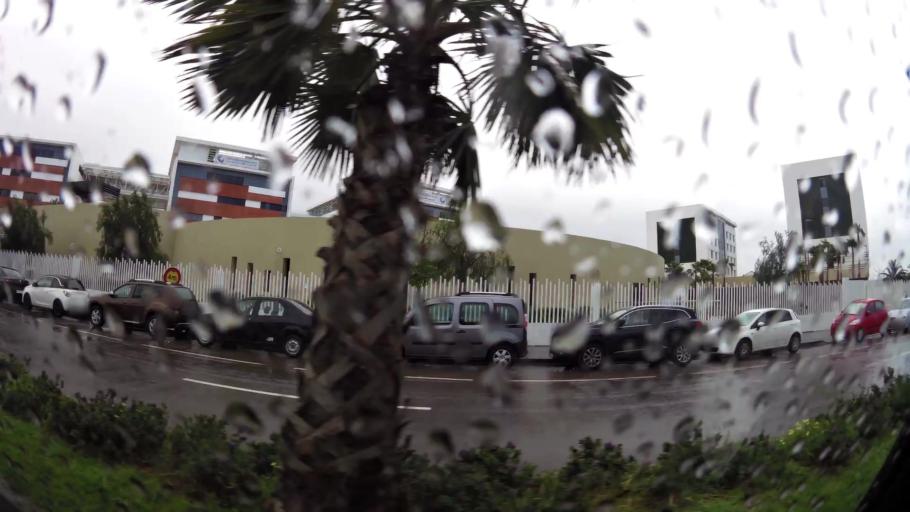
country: MA
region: Grand Casablanca
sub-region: Casablanca
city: Casablanca
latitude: 33.5516
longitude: -7.6676
